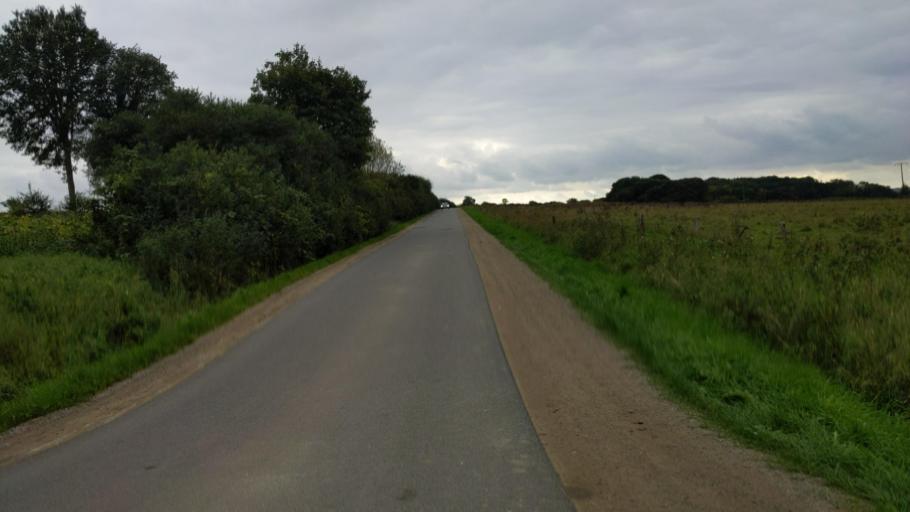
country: DE
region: Schleswig-Holstein
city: Gross Gronau
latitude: 53.7868
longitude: 10.7850
